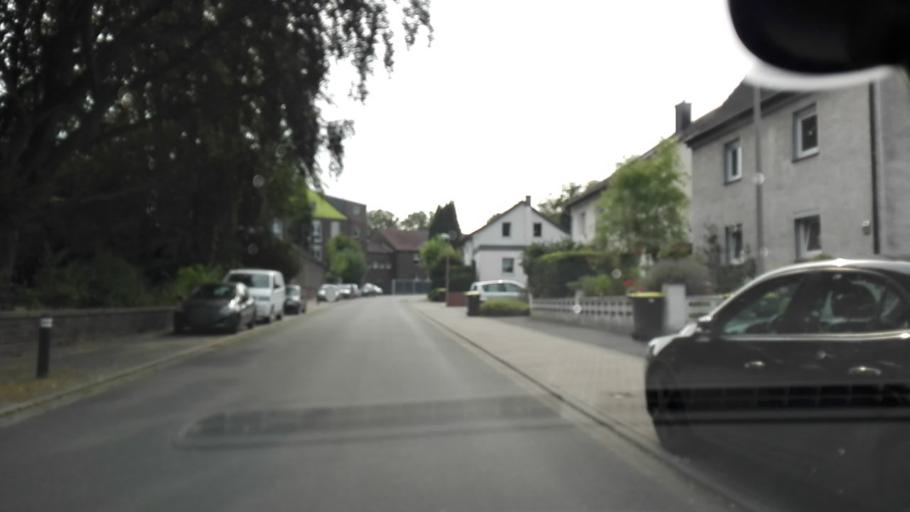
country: DE
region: North Rhine-Westphalia
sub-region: Regierungsbezirk Arnsberg
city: Unna
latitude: 51.5329
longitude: 7.6672
